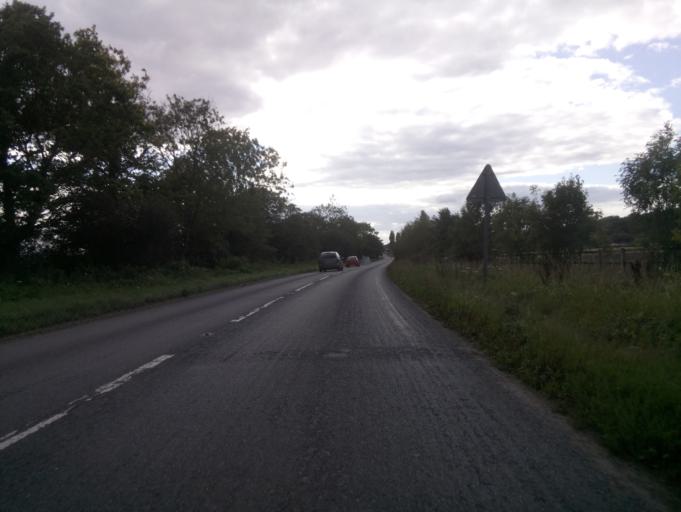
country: GB
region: England
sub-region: Devon
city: Topsham
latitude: 50.7079
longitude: -3.4248
